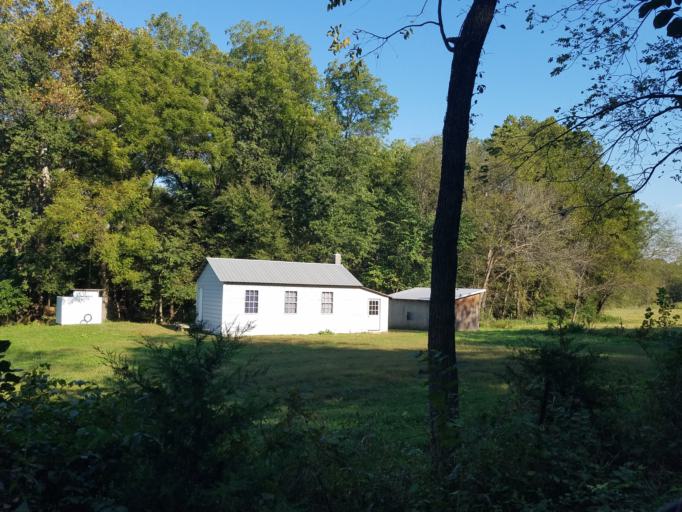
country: US
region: Missouri
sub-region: Moniteau County
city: California
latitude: 38.7469
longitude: -92.6292
